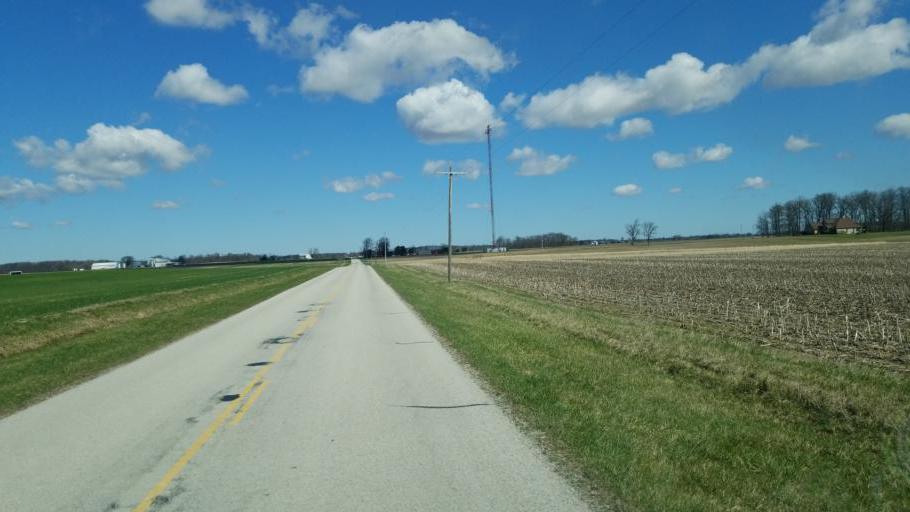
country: US
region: Ohio
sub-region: Sandusky County
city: Mount Carmel
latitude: 41.1939
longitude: -82.9375
